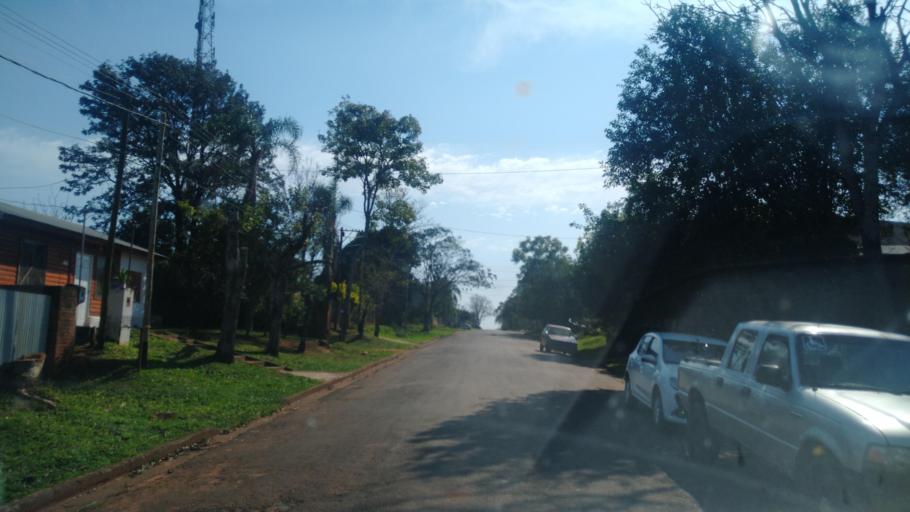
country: AR
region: Misiones
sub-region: Departamento de San Ignacio
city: San Ignacio
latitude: -27.2631
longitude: -55.5417
